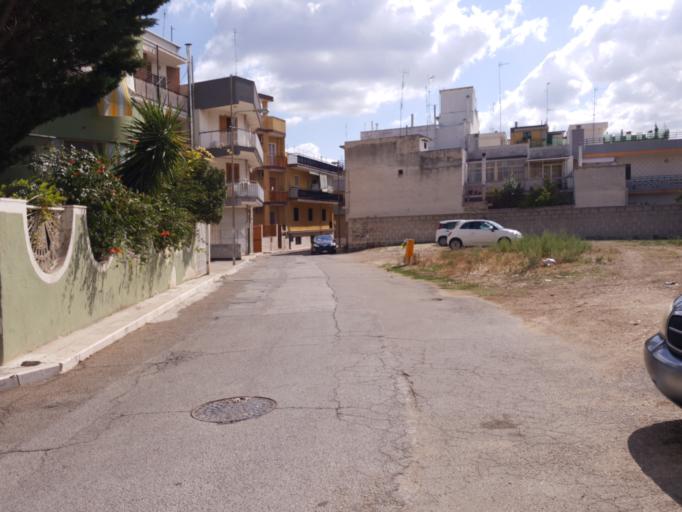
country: IT
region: Apulia
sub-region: Provincia di Bari
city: Triggiano
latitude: 41.0610
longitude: 16.9269
